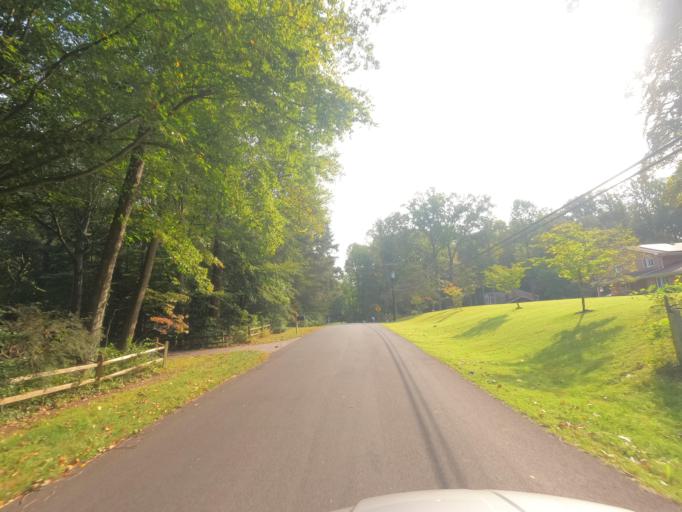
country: US
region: Maryland
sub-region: Prince George's County
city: Bowie
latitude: 38.9702
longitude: -76.7222
